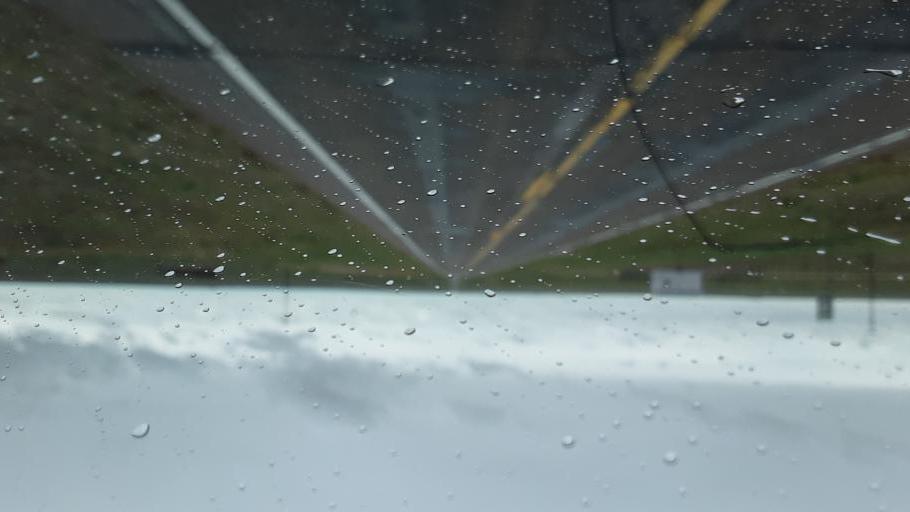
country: US
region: Colorado
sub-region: Lincoln County
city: Hugo
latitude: 38.8494
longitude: -103.2720
